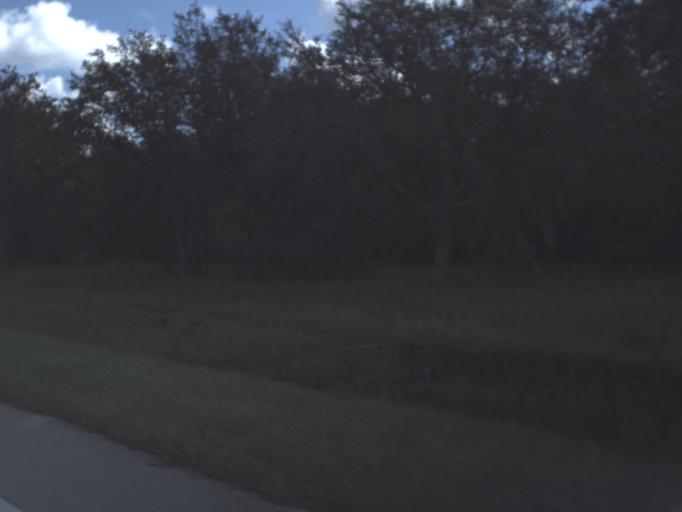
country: US
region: Florida
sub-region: Hendry County
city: Port LaBelle
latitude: 26.8596
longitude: -81.3720
